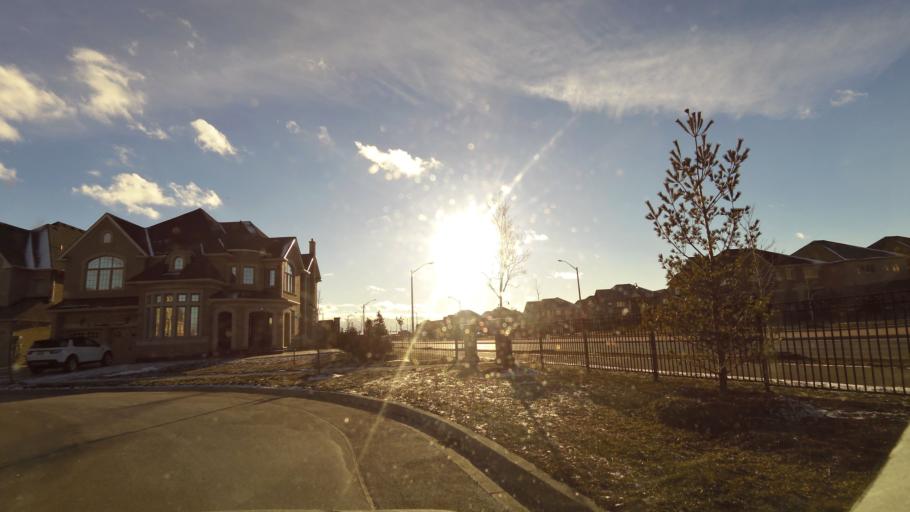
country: CA
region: Ontario
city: Brampton
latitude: 43.6673
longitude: -79.8077
